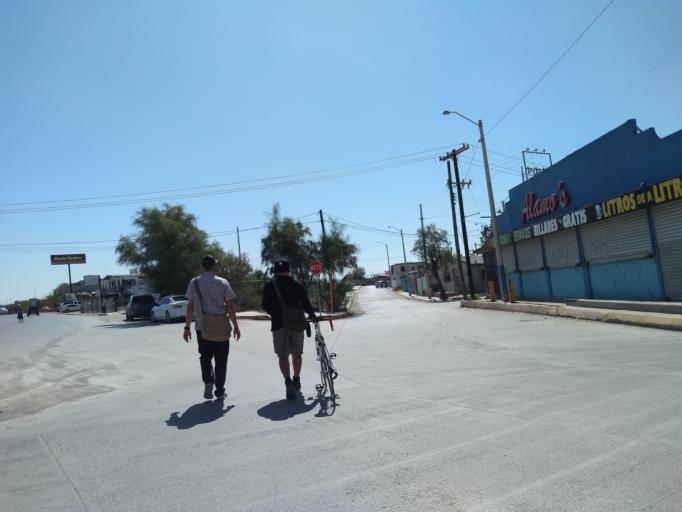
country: US
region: Texas
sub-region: El Paso County
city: El Paso
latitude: 31.7507
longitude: -106.4963
